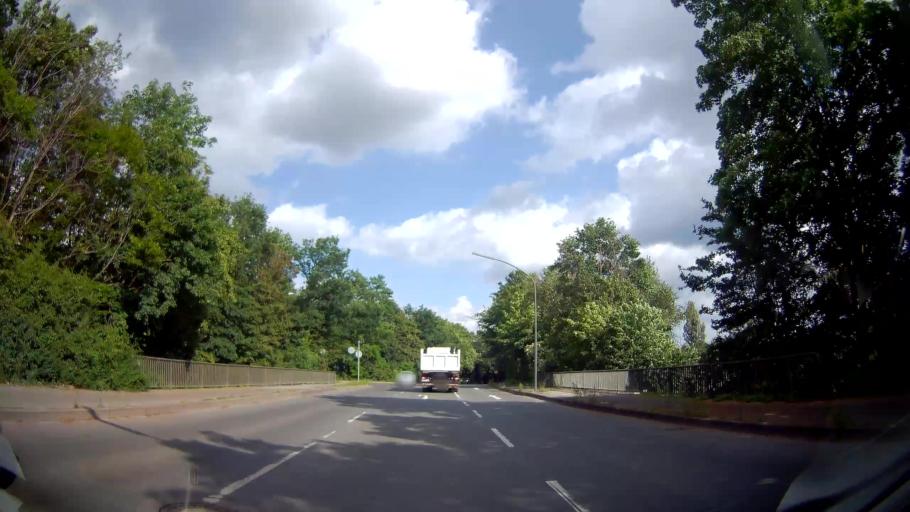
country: DE
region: North Rhine-Westphalia
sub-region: Regierungsbezirk Dusseldorf
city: Essen
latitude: 51.5123
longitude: 7.0465
